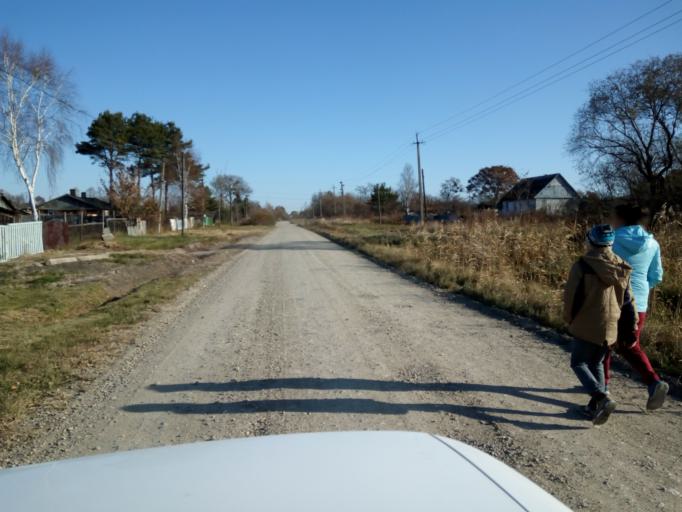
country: RU
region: Primorskiy
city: Lazo
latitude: 45.8680
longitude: 133.6488
